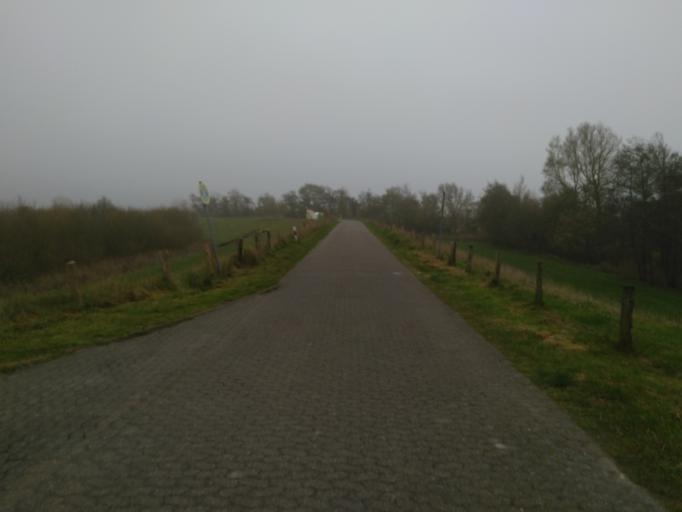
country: DE
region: Schleswig-Holstein
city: Simonsberg
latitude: 54.4548
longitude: 8.9681
